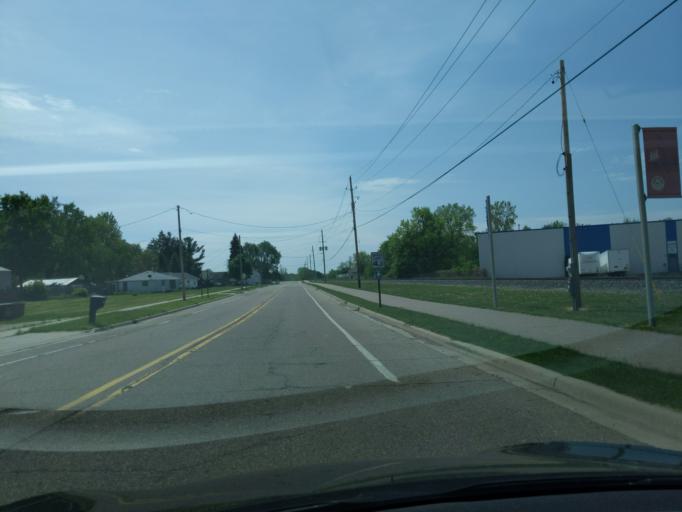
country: US
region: Michigan
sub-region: Ingham County
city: Holt
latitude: 42.6474
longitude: -84.5078
